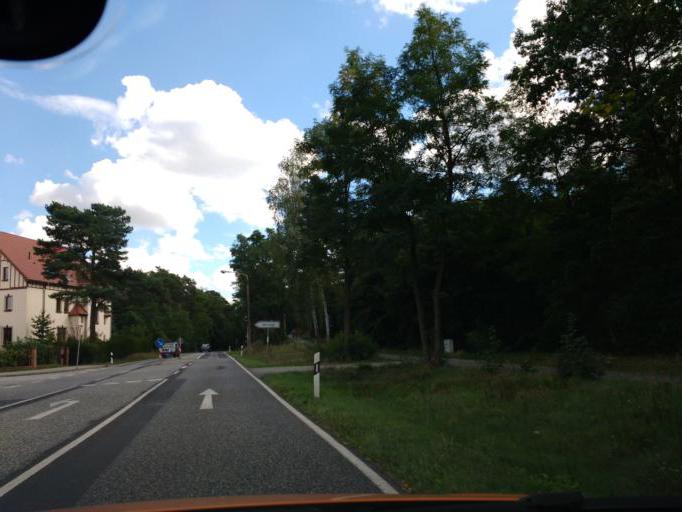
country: DE
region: Brandenburg
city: Wendisch Rietz
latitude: 52.2062
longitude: 14.0085
